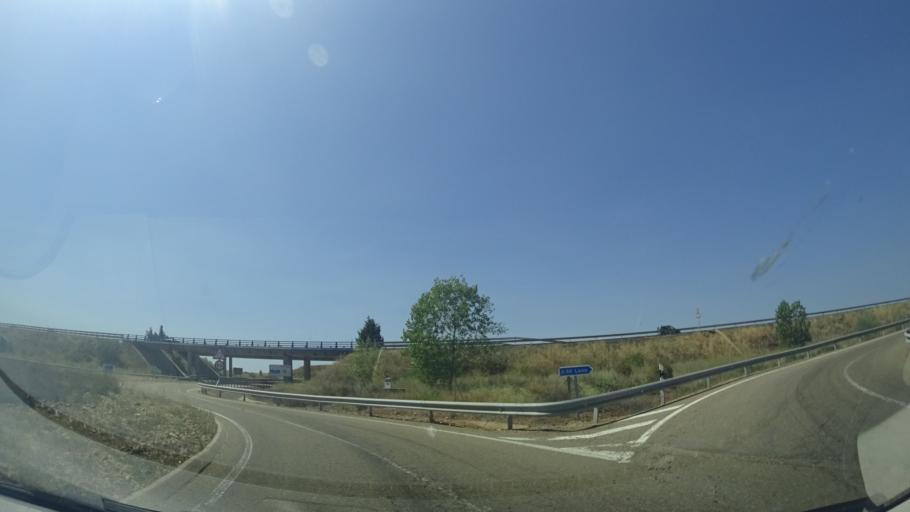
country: ES
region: Castille and Leon
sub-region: Provincia de Leon
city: Ardon
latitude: 42.4396
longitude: -5.5831
